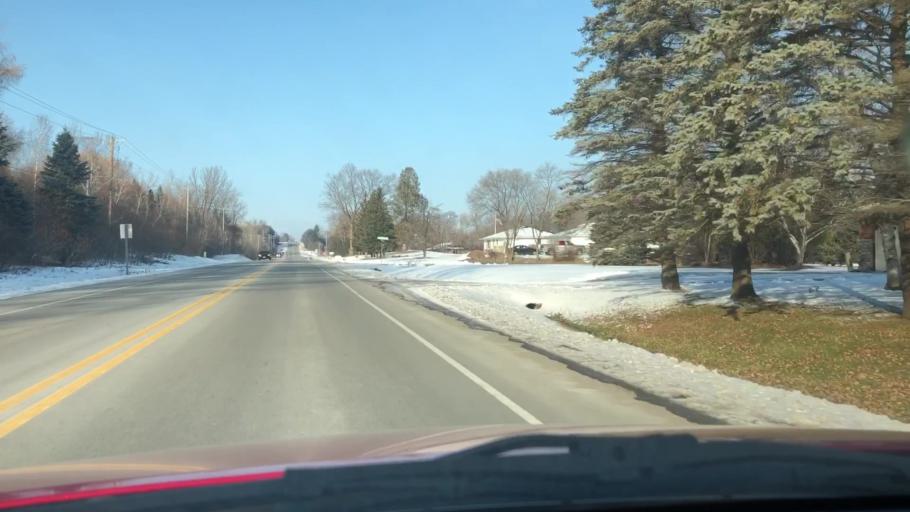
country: US
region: Wisconsin
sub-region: Outagamie County
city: Kimberly
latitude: 44.3206
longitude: -88.3749
